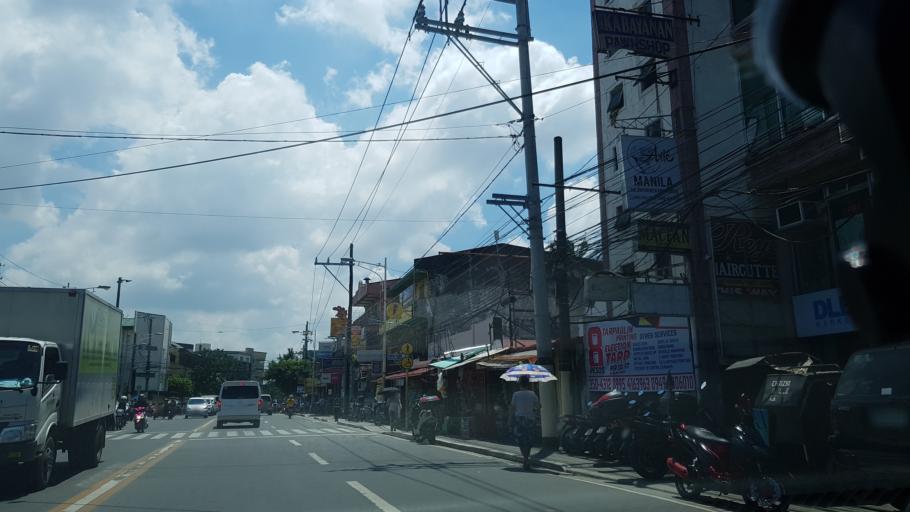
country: PH
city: Sambayanihan People's Village
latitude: 14.4579
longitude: 120.9946
